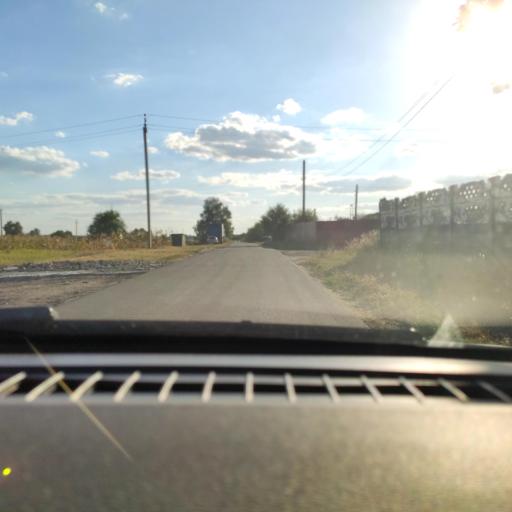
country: RU
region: Voronezj
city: Devitsa
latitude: 51.6472
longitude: 38.9489
